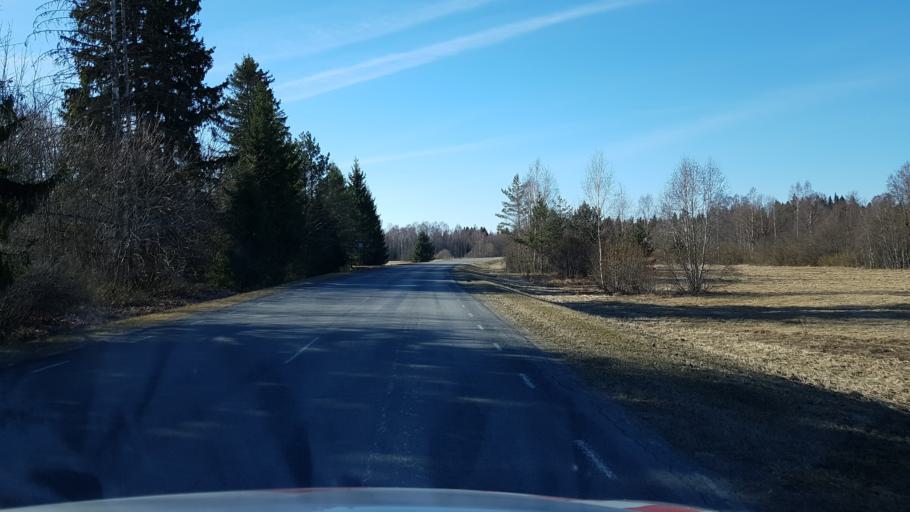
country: EE
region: Harju
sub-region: Keila linn
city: Keila
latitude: 59.2406
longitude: 24.4673
